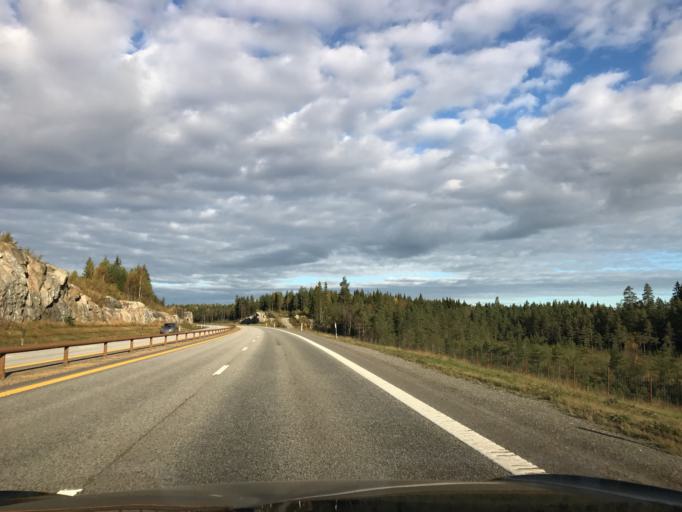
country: NO
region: Akershus
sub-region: Eidsvoll
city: Raholt
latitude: 60.2642
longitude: 11.1707
